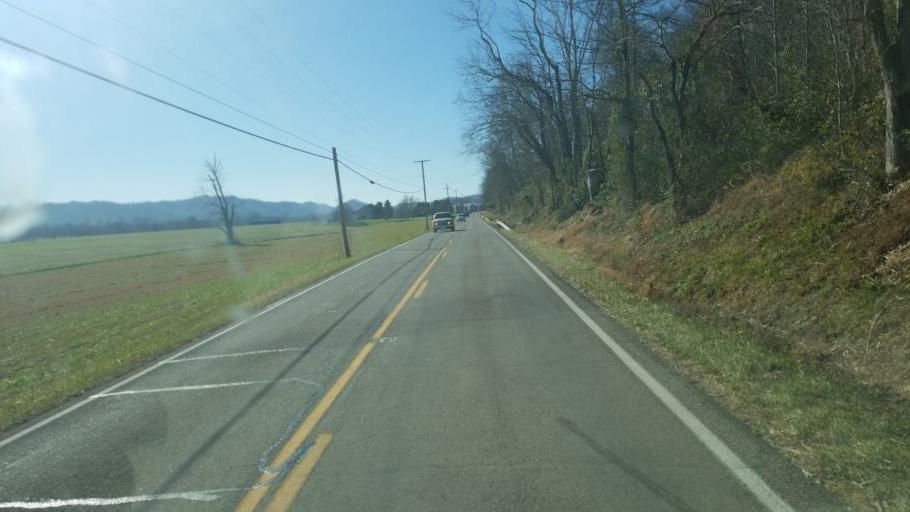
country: US
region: Ohio
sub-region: Scioto County
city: West Portsmouth
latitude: 38.6363
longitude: -83.1468
